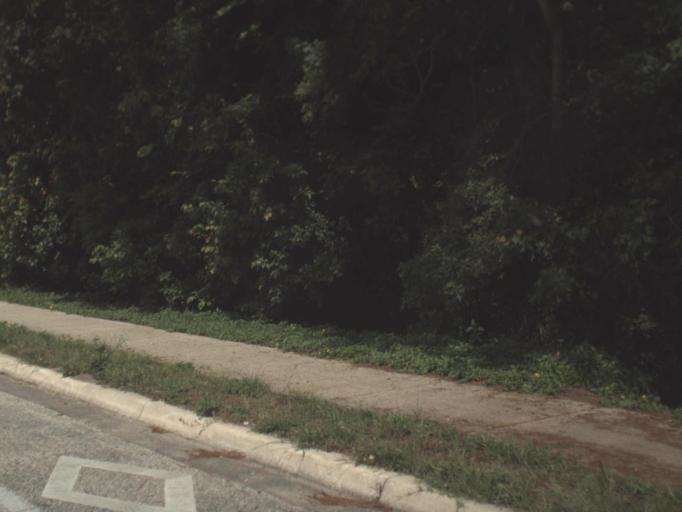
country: US
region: Florida
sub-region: Saint Johns County
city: Saint Augustine
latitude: 29.8725
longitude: -81.3342
